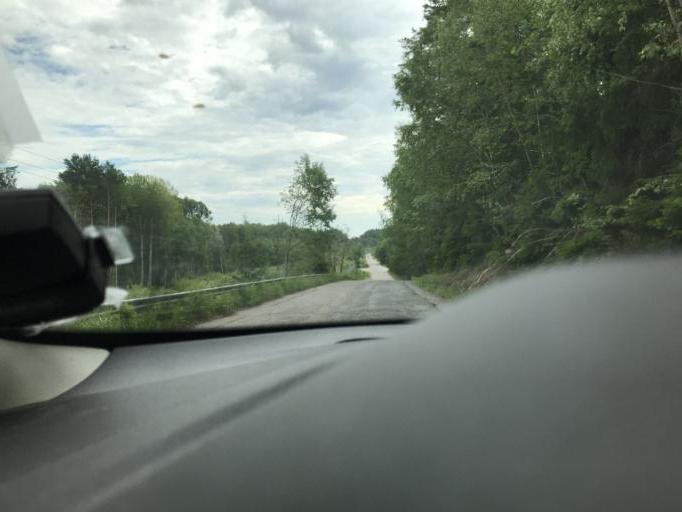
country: SE
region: Stockholm
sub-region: Botkyrka Kommun
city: Varsta
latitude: 59.1950
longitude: 17.7864
